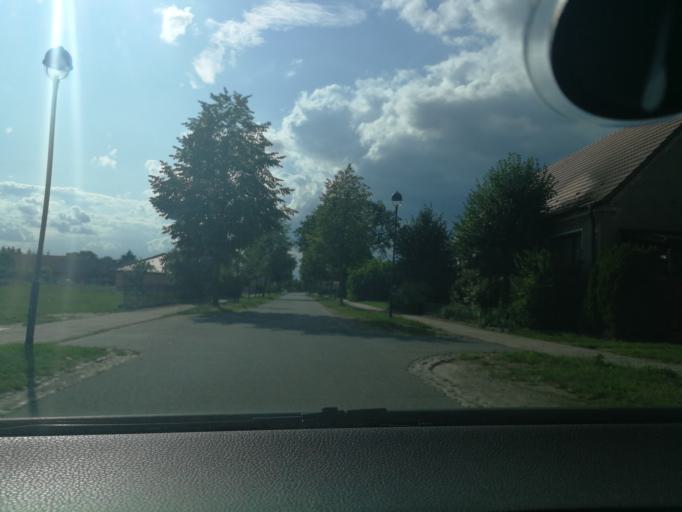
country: DE
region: Brandenburg
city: Gerdshagen
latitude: 53.2070
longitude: 12.2041
